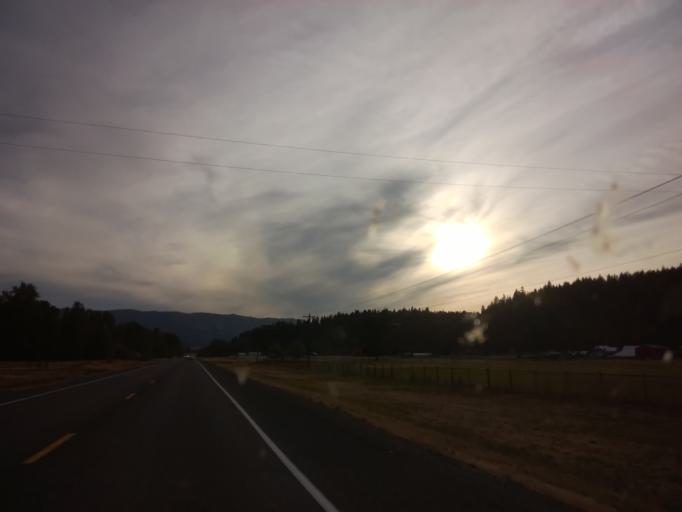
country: US
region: Washington
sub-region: Kittitas County
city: Cle Elum
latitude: 47.1897
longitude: -120.8159
